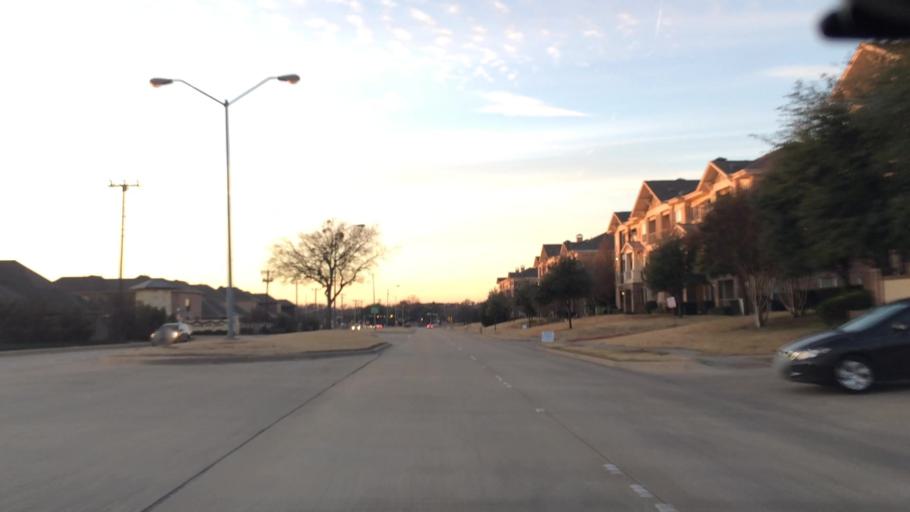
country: US
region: Texas
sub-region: Collin County
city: Frisco
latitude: 33.0911
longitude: -96.7970
